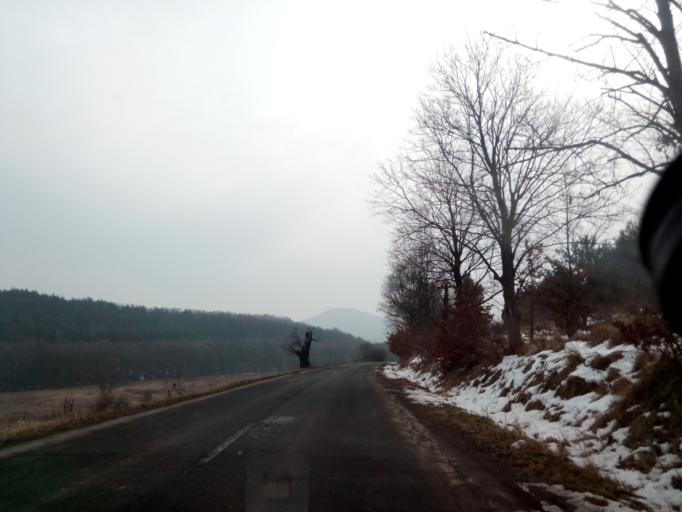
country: HU
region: Borsod-Abauj-Zemplen
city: Gonc
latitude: 48.5016
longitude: 21.3387
